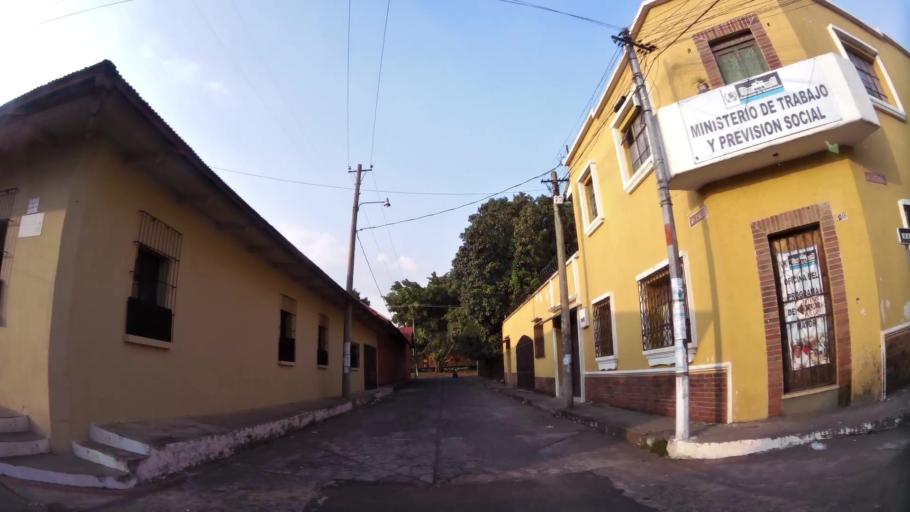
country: GT
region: Retalhuleu
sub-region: Municipio de Retalhuleu
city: Retalhuleu
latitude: 14.5373
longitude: -91.6808
